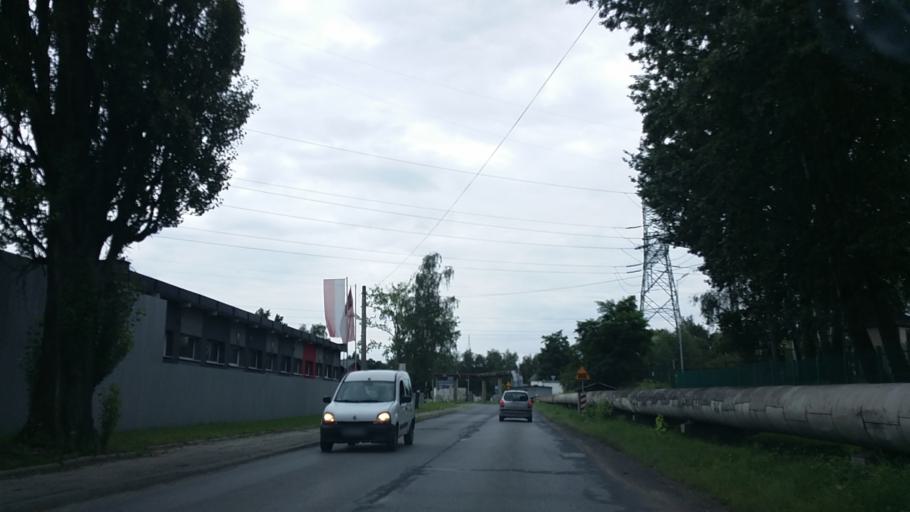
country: PL
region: Lesser Poland Voivodeship
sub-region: Powiat krakowski
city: Skawina
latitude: 49.9754
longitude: 19.8091
